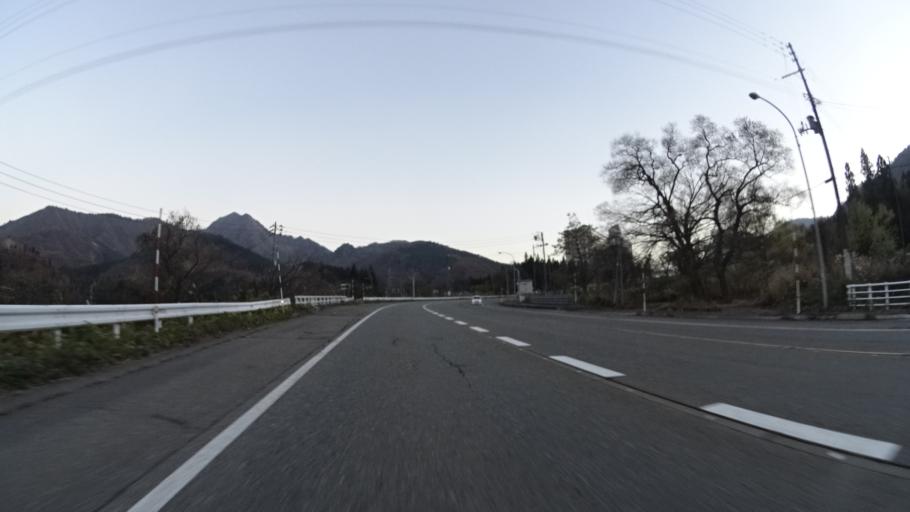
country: JP
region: Niigata
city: Shiozawa
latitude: 36.9717
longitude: 138.8012
